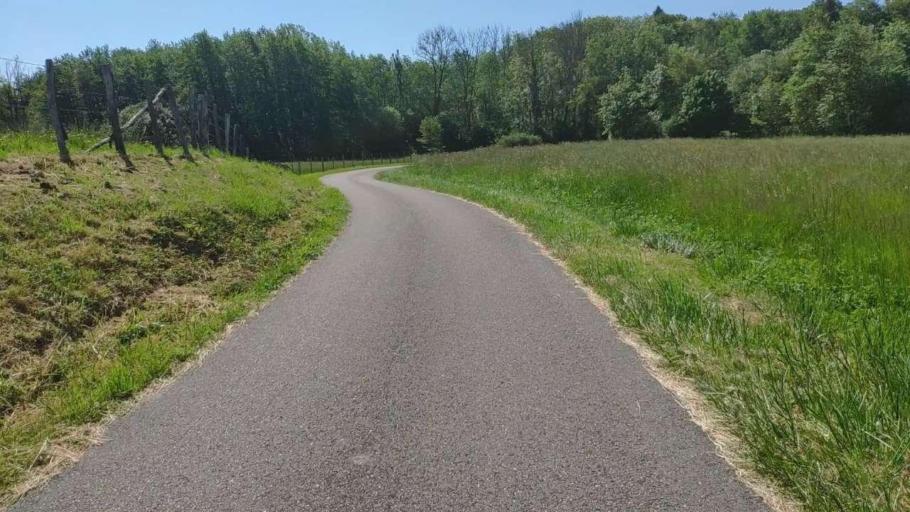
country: FR
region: Franche-Comte
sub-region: Departement du Jura
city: Bletterans
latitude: 46.7787
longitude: 5.4235
